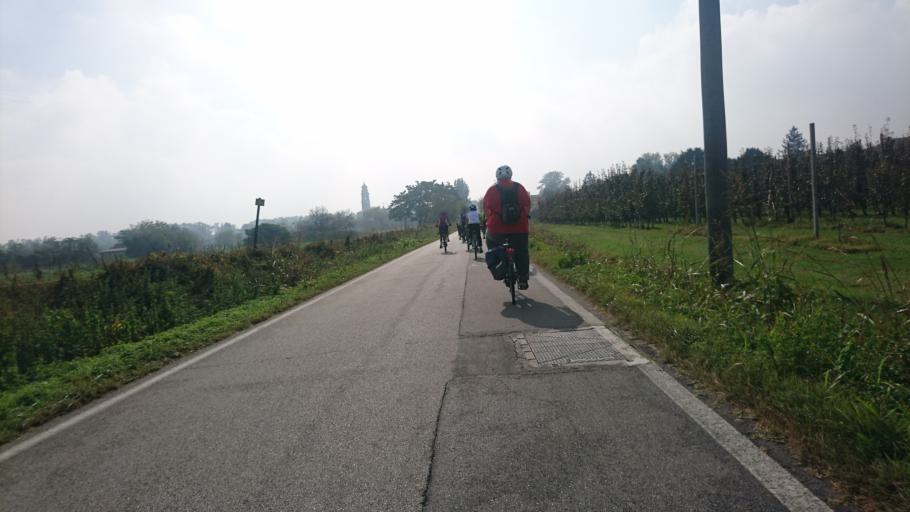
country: IT
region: Veneto
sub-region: Provincia di Padova
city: Boara Pisani
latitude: 45.1135
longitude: 11.7856
